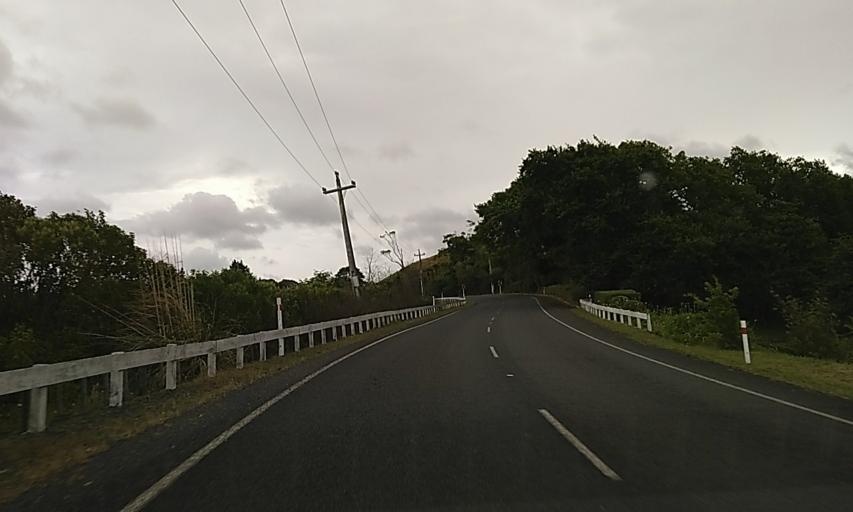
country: NZ
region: Auckland
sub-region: Auckland
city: Pukekohe East
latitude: -37.3093
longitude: 174.9381
